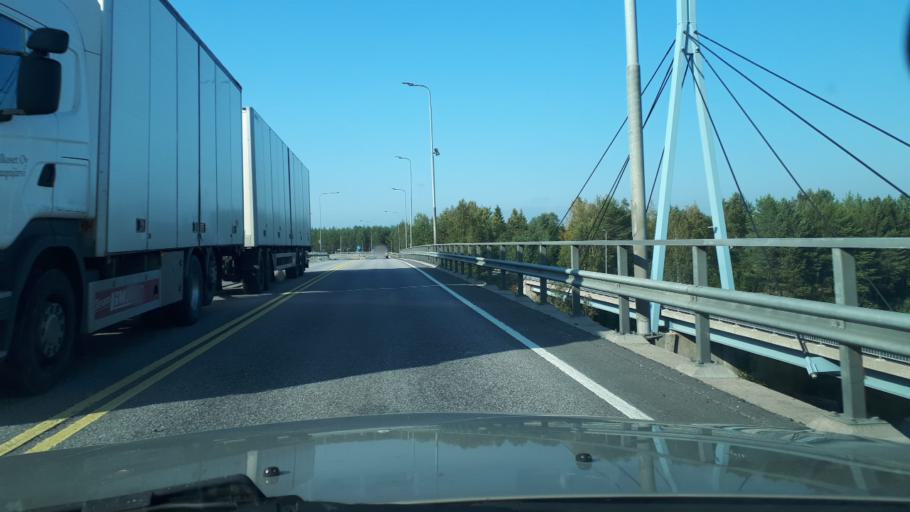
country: FI
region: Northern Ostrobothnia
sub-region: Oulunkaari
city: Ii
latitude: 65.3309
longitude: 25.3772
